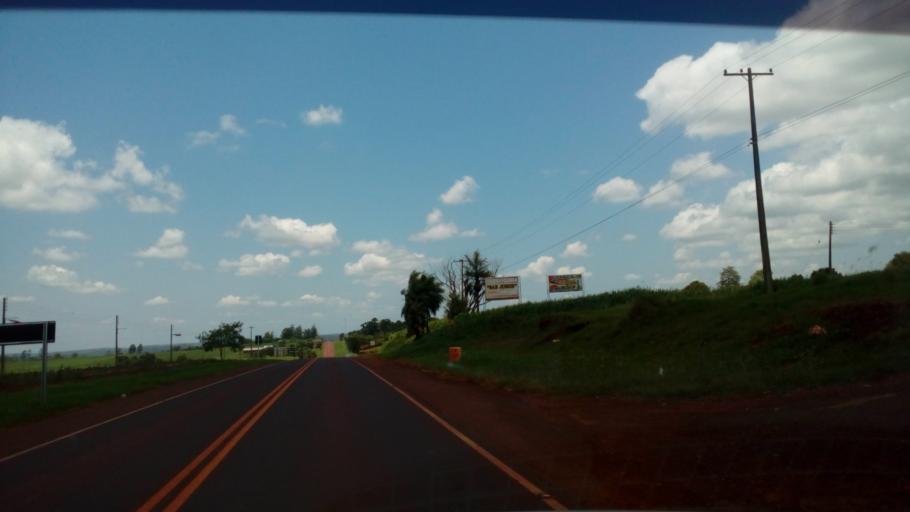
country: PY
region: Itapua
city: Arquitecto Tomas Romero Pereira
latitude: -26.3681
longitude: -55.2393
